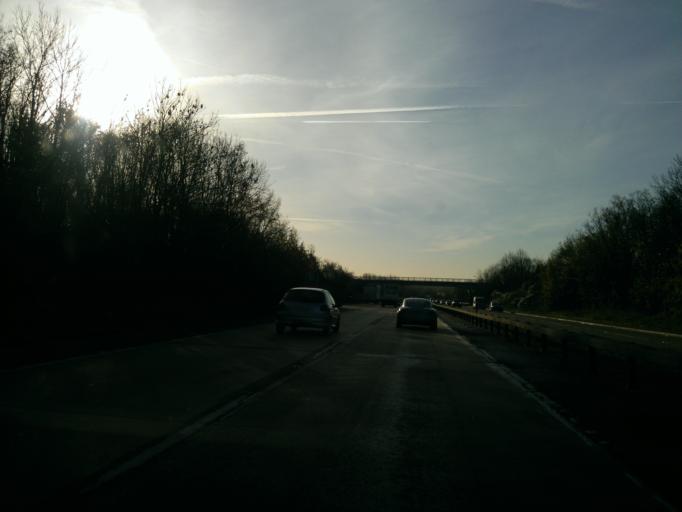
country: GB
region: England
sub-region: Essex
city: Kelvedon
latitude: 51.8453
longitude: 0.7241
